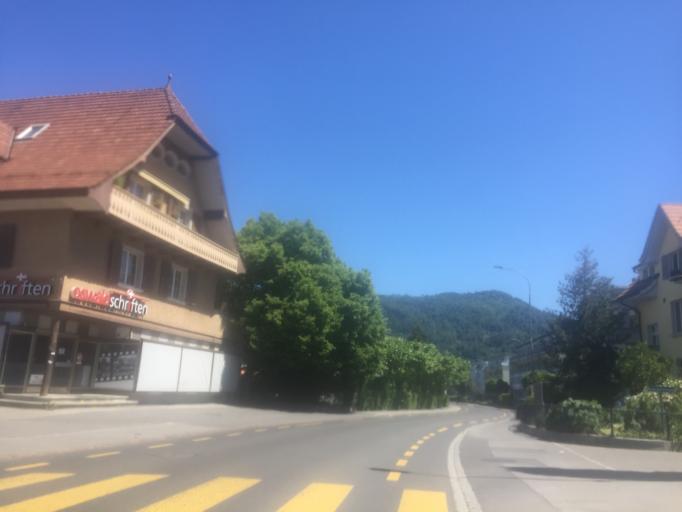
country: CH
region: Bern
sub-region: Thun District
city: Thun
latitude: 46.7513
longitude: 7.6202
